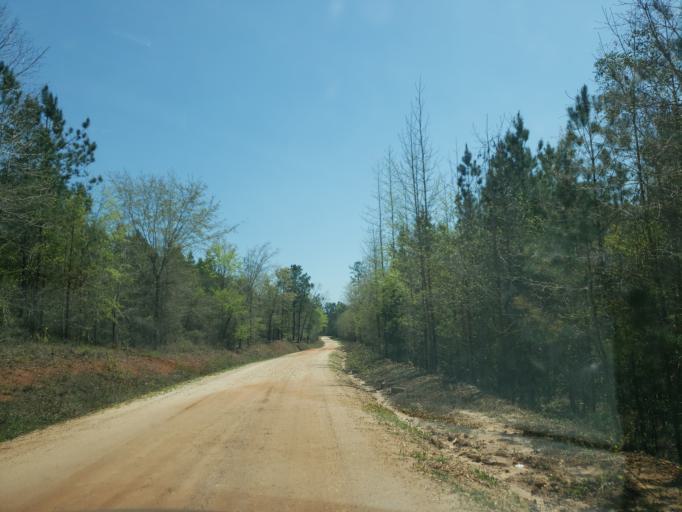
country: US
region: Alabama
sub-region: Tallapoosa County
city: Camp Hill
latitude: 32.6779
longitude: -85.6659
